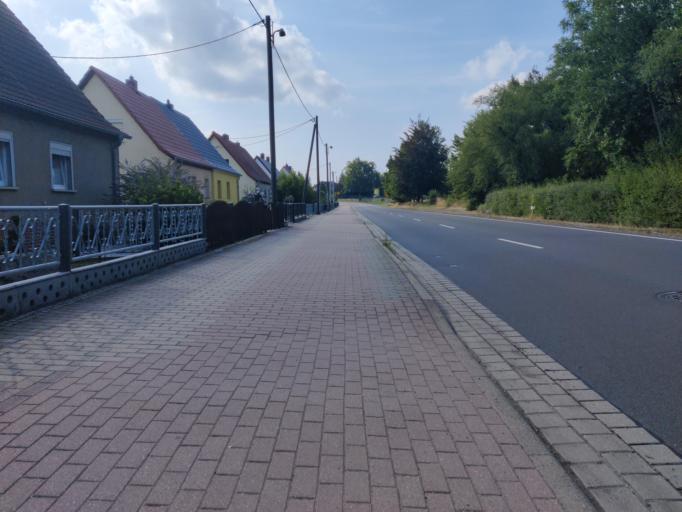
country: DE
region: Saxony
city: Deutzen
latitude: 51.1127
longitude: 12.4238
